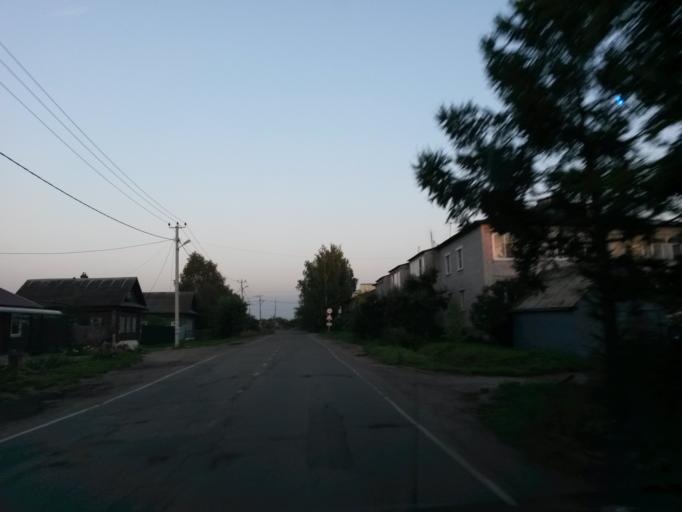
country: RU
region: Jaroslavl
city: Tutayev
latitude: 57.8789
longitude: 39.5585
